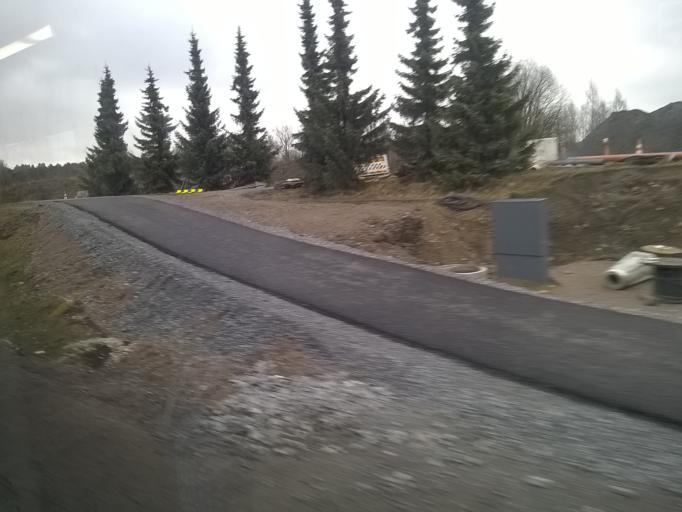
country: FI
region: Pirkanmaa
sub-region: Tampere
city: Tampere
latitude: 61.4899
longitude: 23.8246
